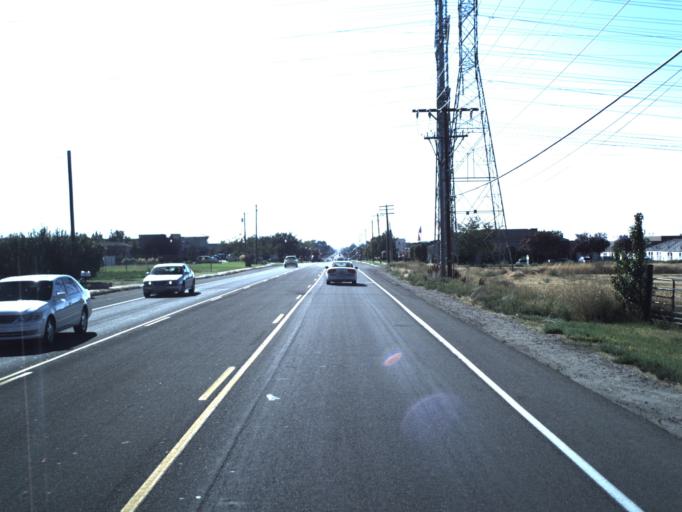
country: US
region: Utah
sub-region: Davis County
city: Clinton
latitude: 41.1399
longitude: -112.0569
